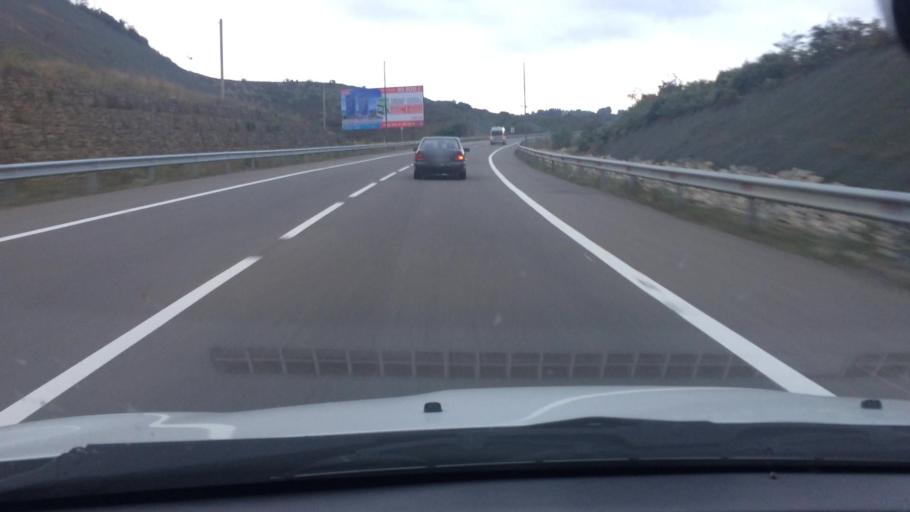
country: GE
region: Ajaria
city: Makhinjauri
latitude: 41.7242
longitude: 41.7493
